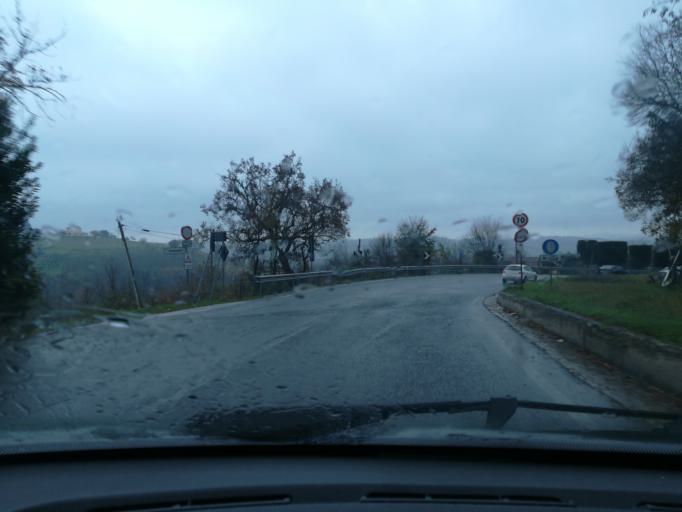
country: IT
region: The Marches
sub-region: Provincia di Macerata
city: Macerata
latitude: 43.2827
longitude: 13.4331
